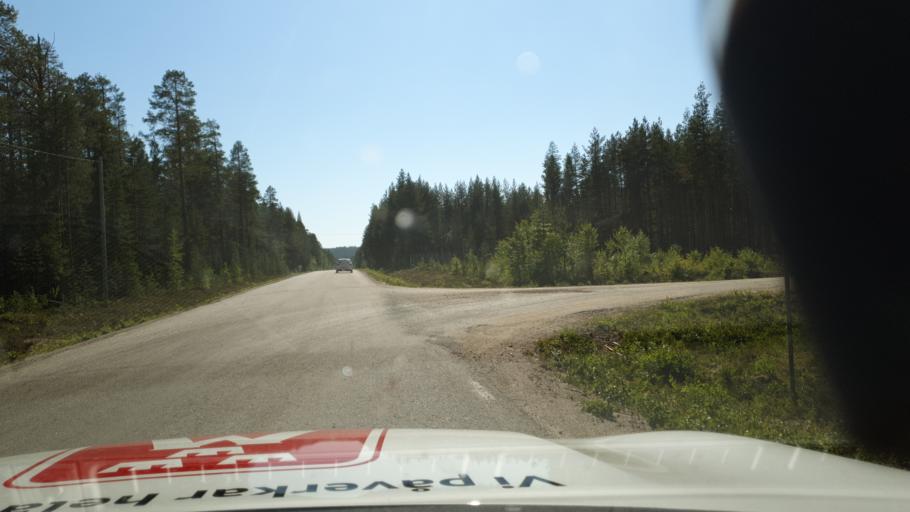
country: SE
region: Vaesterbotten
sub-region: Vindelns Kommun
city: Vindeln
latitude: 64.2326
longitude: 19.7872
